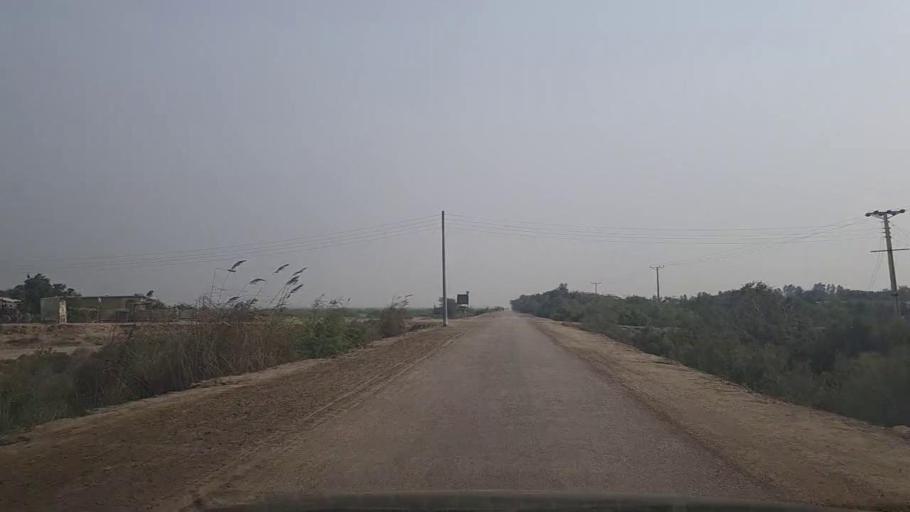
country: PK
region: Sindh
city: Mirpur Sakro
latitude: 24.4710
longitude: 67.6742
